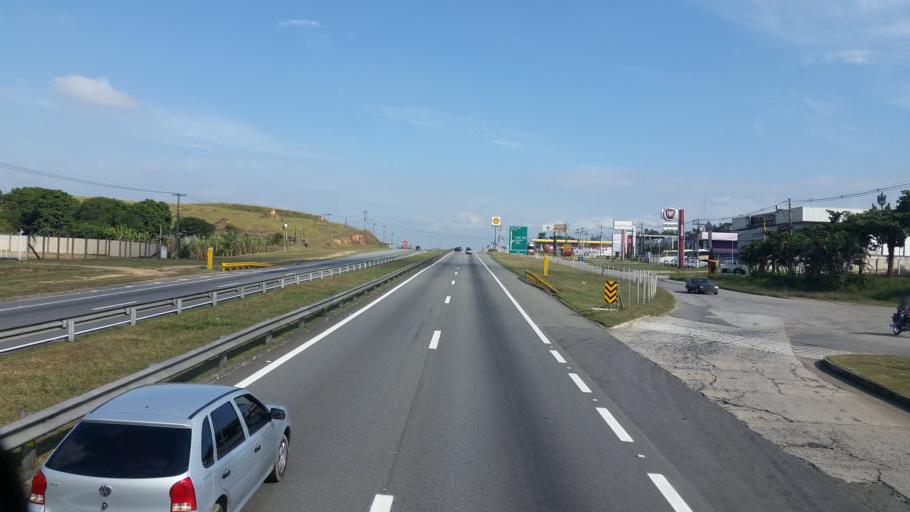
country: BR
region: Rio de Janeiro
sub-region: Resende
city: Resende
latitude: -22.4577
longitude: -44.4187
